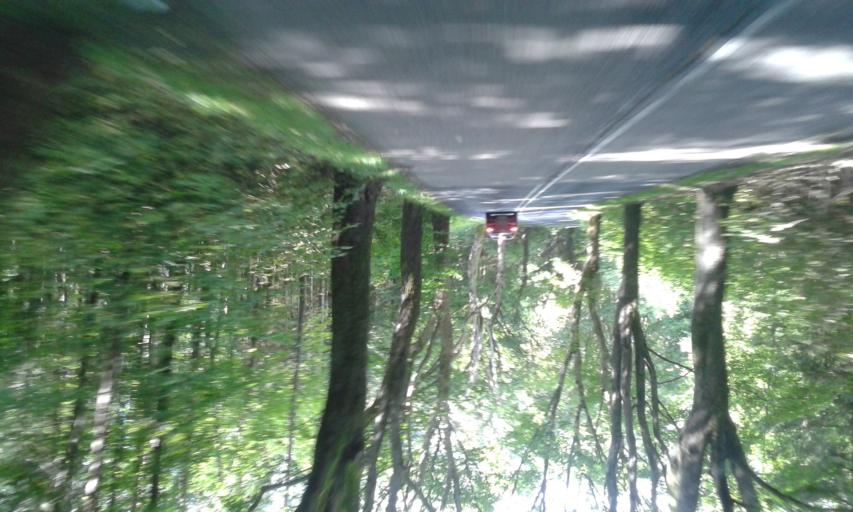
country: PL
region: West Pomeranian Voivodeship
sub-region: Powiat koszalinski
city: Polanow
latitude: 54.2288
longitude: 16.6986
